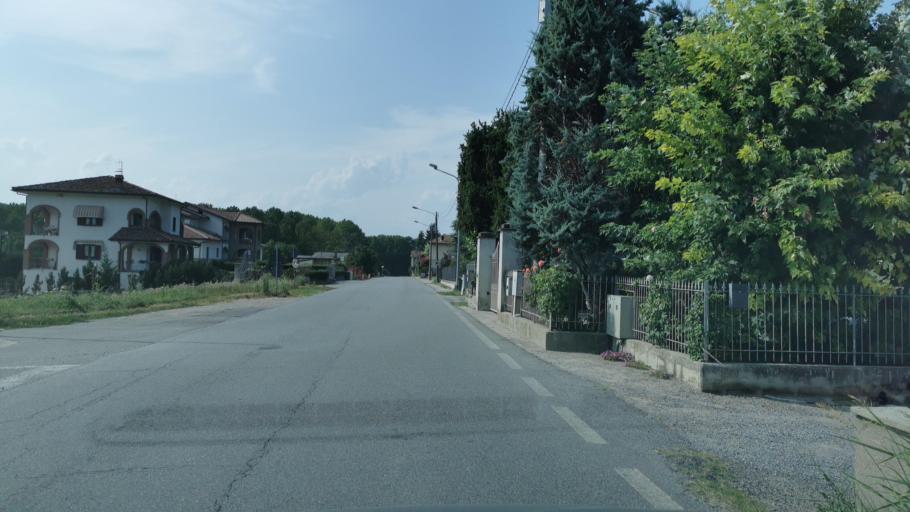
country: IT
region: Piedmont
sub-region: Provincia di Cuneo
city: Grinzane Cavour
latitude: 44.6454
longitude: 7.9980
